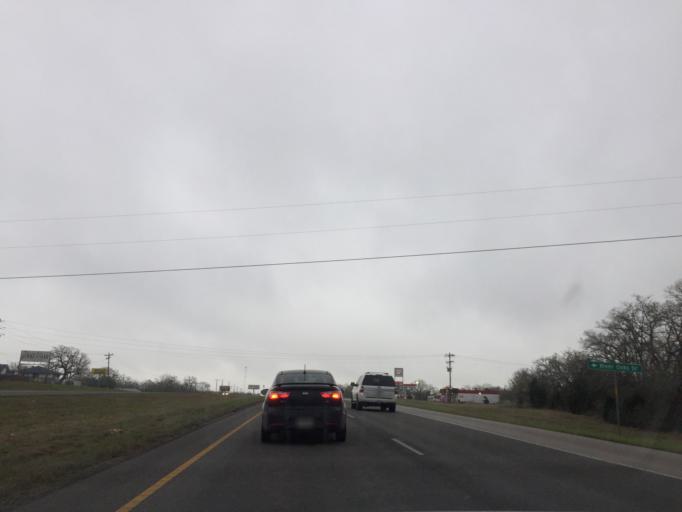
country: US
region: Texas
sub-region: Bastrop County
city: Wyldwood
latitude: 30.1296
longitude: -97.4457
